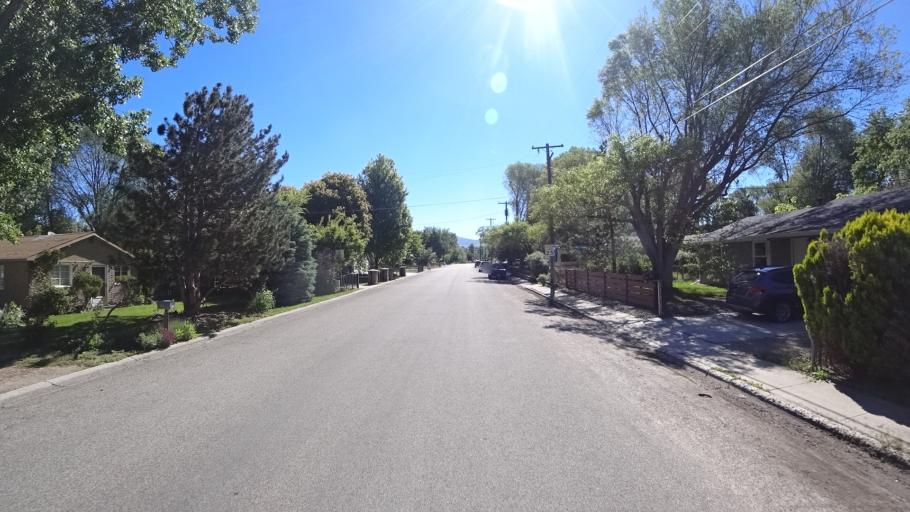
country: US
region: Idaho
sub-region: Ada County
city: Garden City
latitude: 43.6483
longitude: -116.2383
